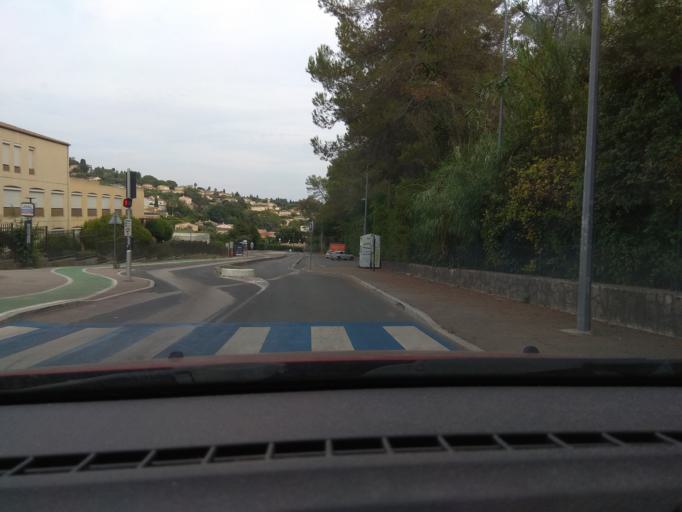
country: FR
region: Provence-Alpes-Cote d'Azur
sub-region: Departement des Alpes-Maritimes
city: La Colle-sur-Loup
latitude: 43.6844
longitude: 7.1024
